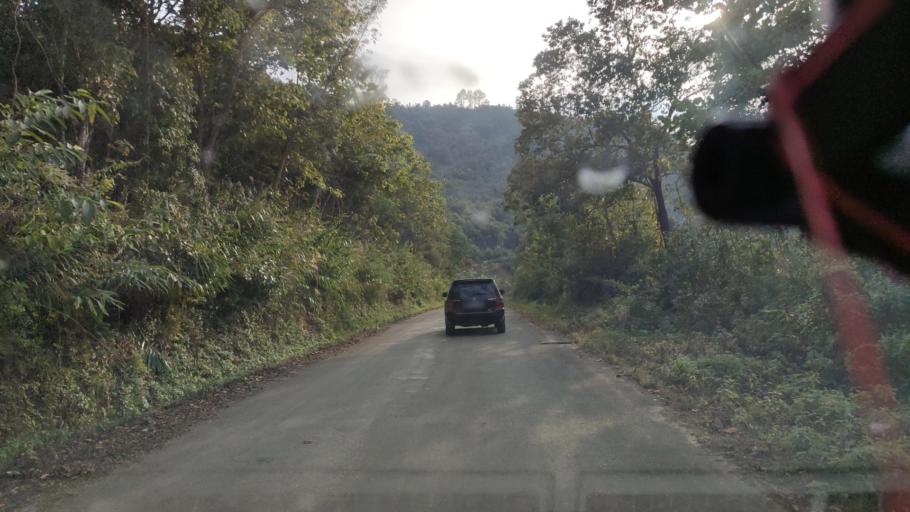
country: CN
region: Yunnan
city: Menghai
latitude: 21.4584
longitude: 99.7073
